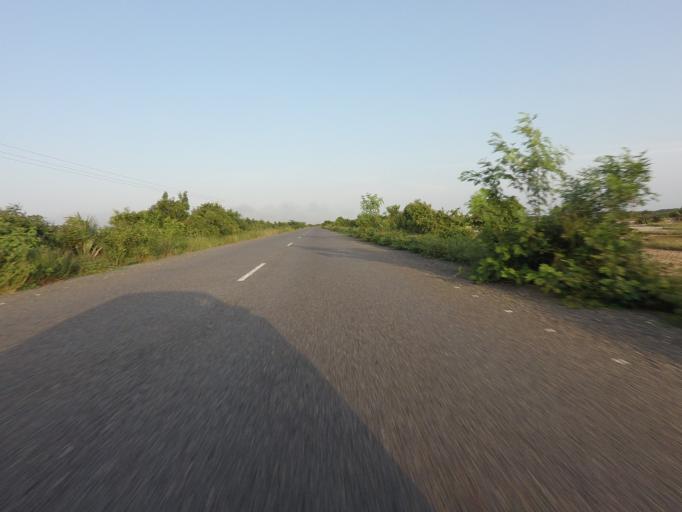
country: GH
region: Volta
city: Anloga
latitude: 5.8469
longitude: 0.7780
